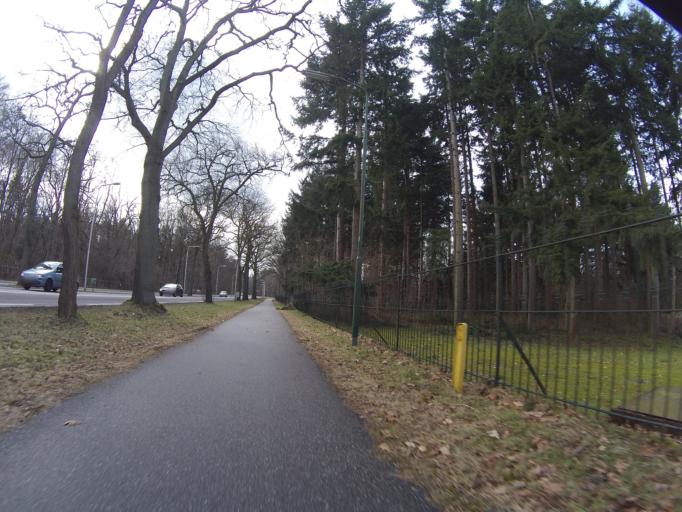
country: NL
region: Utrecht
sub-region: Gemeente Soest
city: Soest
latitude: 52.1429
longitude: 5.2967
